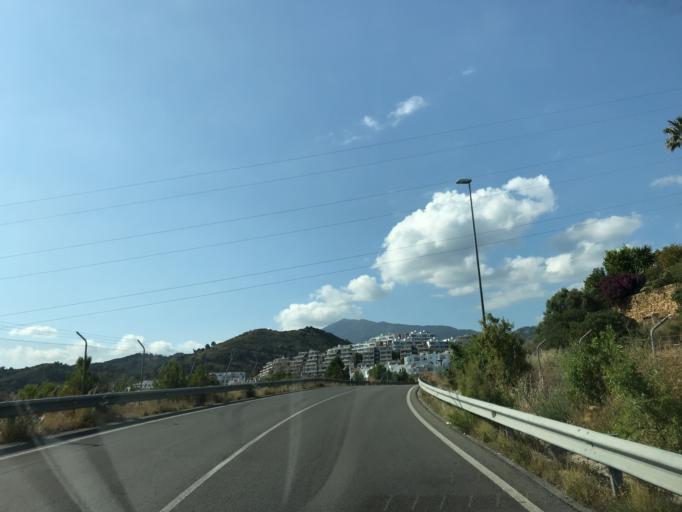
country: ES
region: Andalusia
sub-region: Provincia de Malaga
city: Benahavis
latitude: 36.5012
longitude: -5.0153
